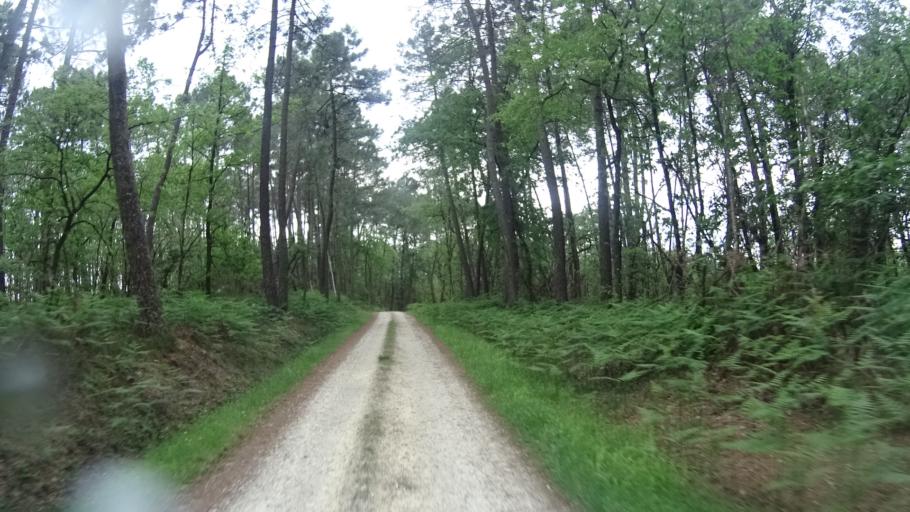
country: FR
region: Aquitaine
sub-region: Departement de la Dordogne
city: Sourzac
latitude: 45.0310
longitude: 0.4451
